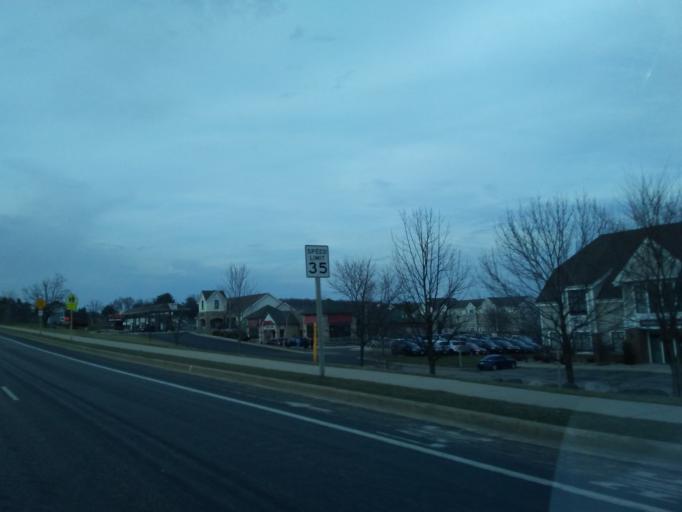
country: US
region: Wisconsin
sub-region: Dane County
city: Verona
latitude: 43.0019
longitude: -89.5337
